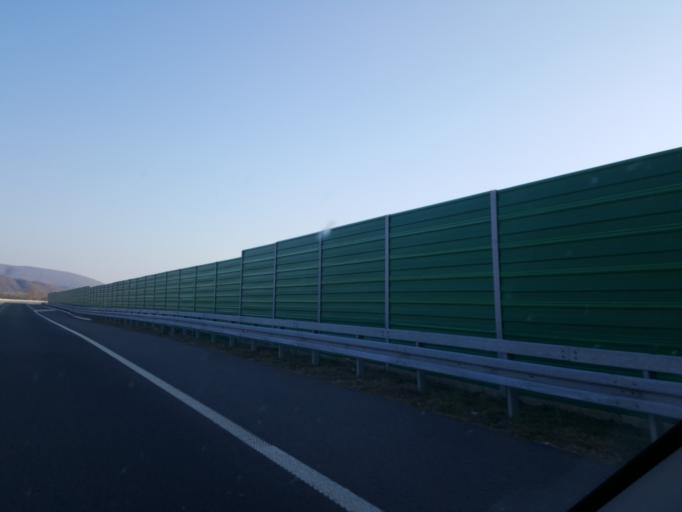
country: RS
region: Central Serbia
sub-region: Pirotski Okrug
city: Pirot
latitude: 43.0732
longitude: 22.6721
